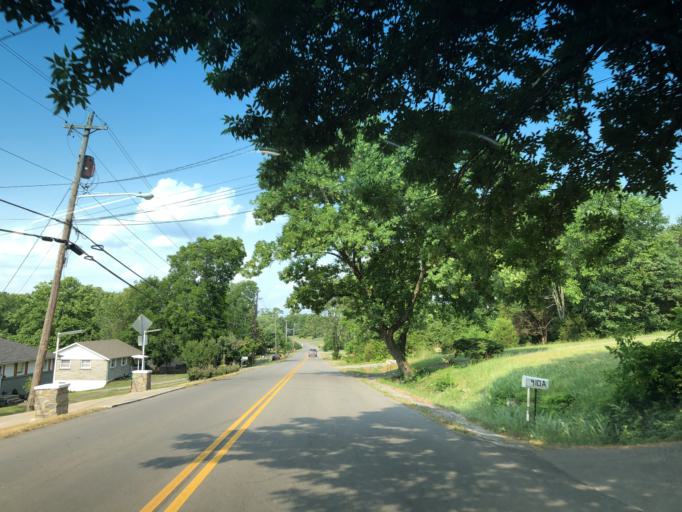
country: US
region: Tennessee
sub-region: Davidson County
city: Goodlettsville
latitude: 36.2777
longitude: -86.7281
